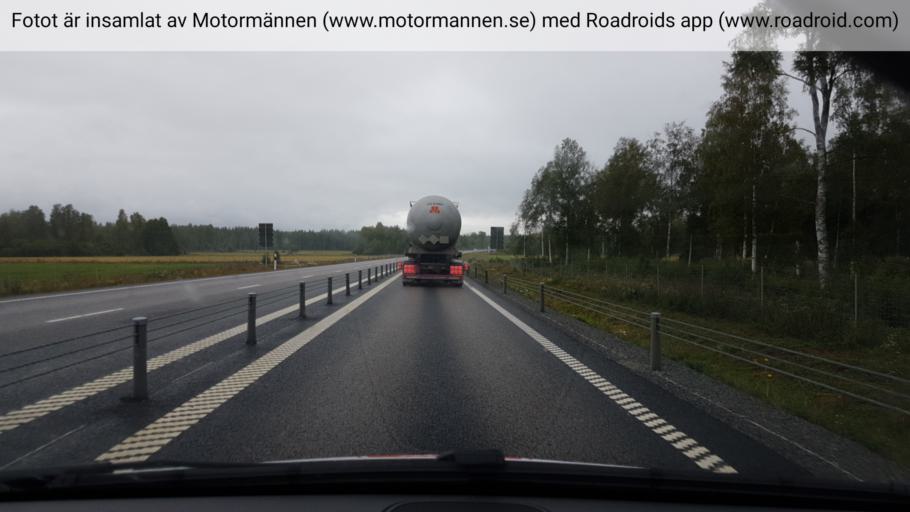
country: SE
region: Uppsala
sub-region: Heby Kommun
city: Heby
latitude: 60.0008
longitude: 16.8521
